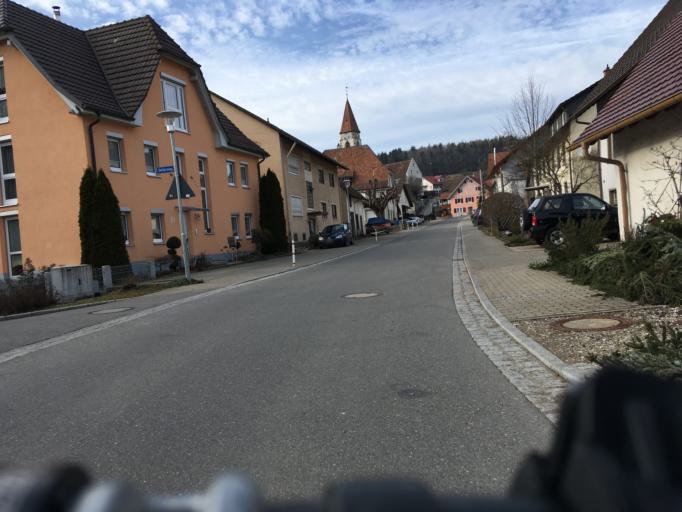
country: DE
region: Baden-Wuerttemberg
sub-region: Freiburg Region
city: Tengen
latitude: 47.7919
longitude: 8.6866
